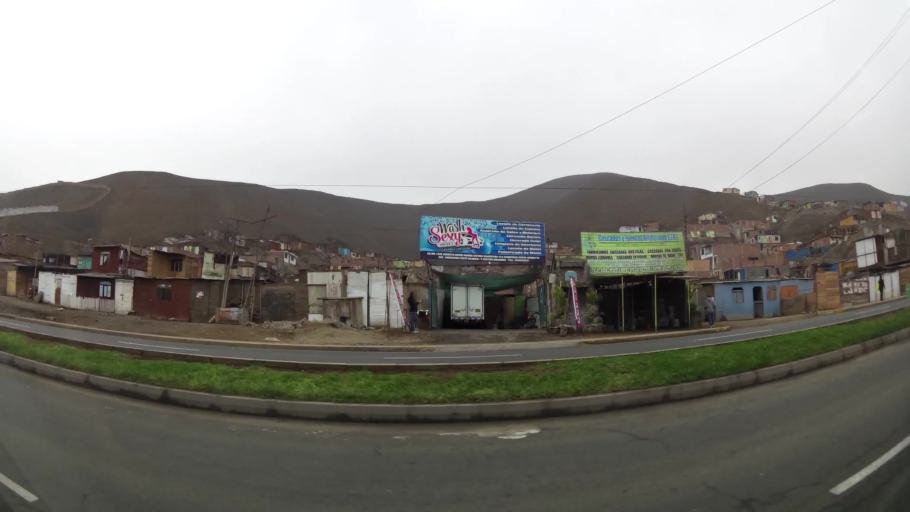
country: PE
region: Lima
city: Ventanilla
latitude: -11.8907
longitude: -77.1260
